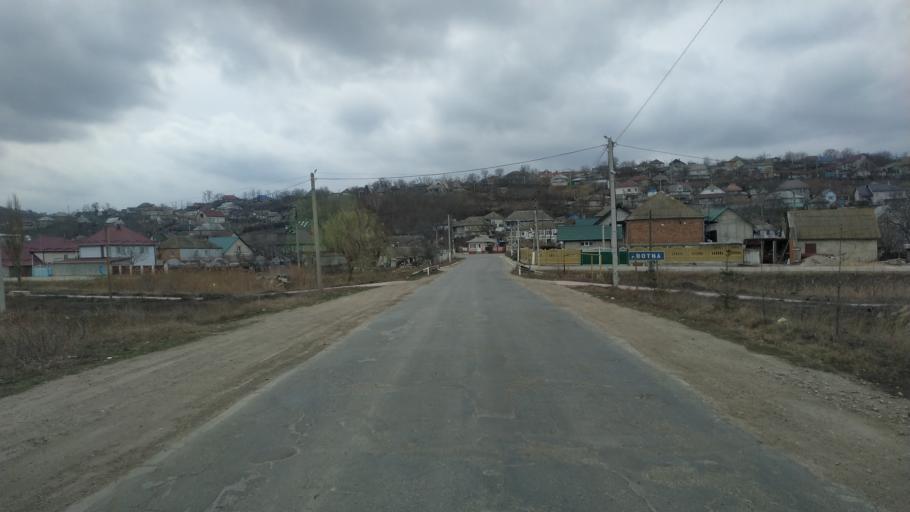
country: MD
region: Laloveni
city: Ialoveni
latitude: 46.8745
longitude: 28.7635
